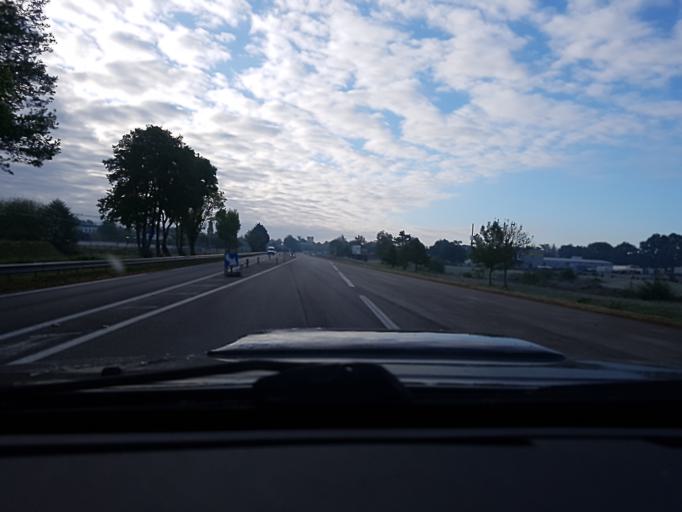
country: FR
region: Pays de la Loire
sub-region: Departement de la Vendee
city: Aizenay
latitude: 46.7509
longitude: -1.6293
